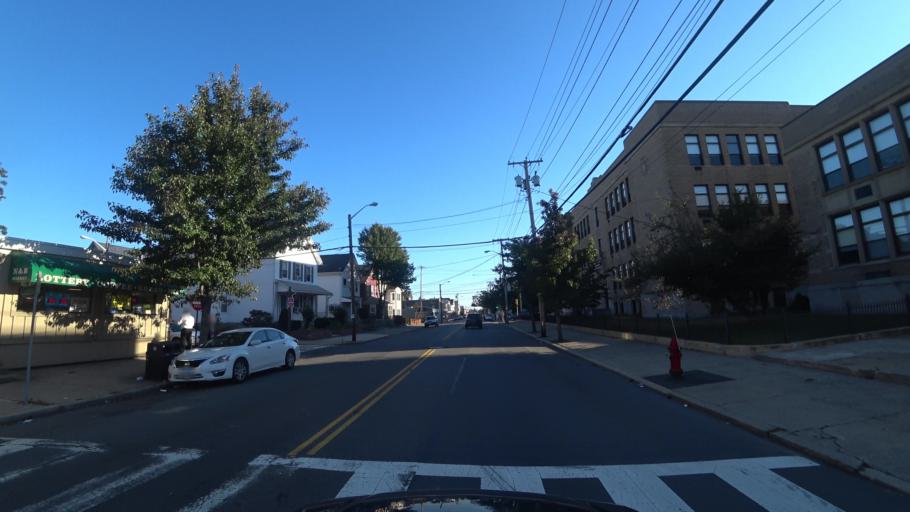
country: US
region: Massachusetts
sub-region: Middlesex County
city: Malden
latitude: 42.4242
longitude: -71.0807
